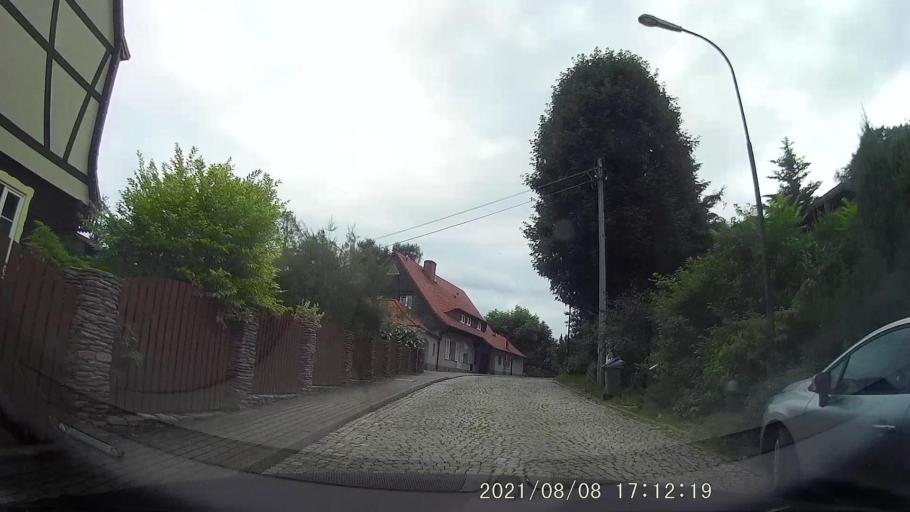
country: PL
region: Lower Silesian Voivodeship
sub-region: Powiat klodzki
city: Duszniki-Zdroj
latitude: 50.4007
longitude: 16.3859
